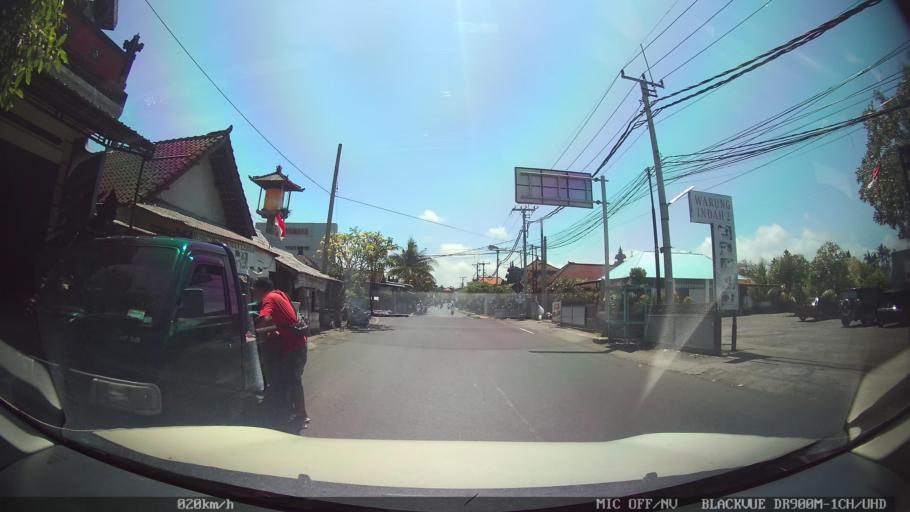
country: ID
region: Bali
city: Klungkung
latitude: -8.5796
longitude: 115.3548
